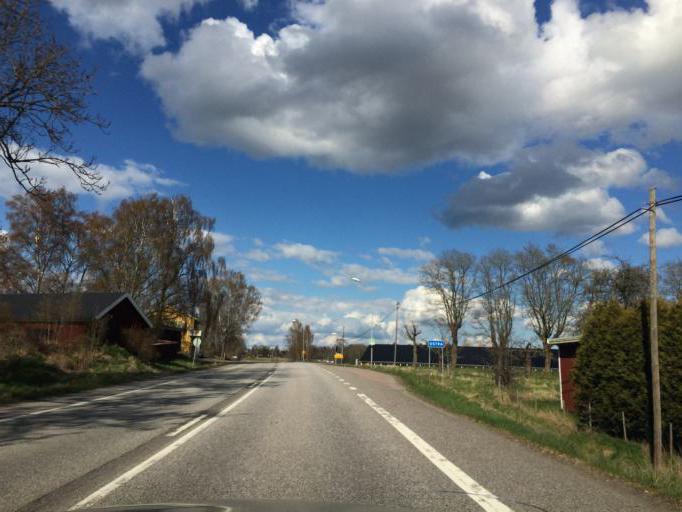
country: SE
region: Soedermanland
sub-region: Eskilstuna Kommun
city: Eskilstuna
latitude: 59.4248
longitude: 16.6067
